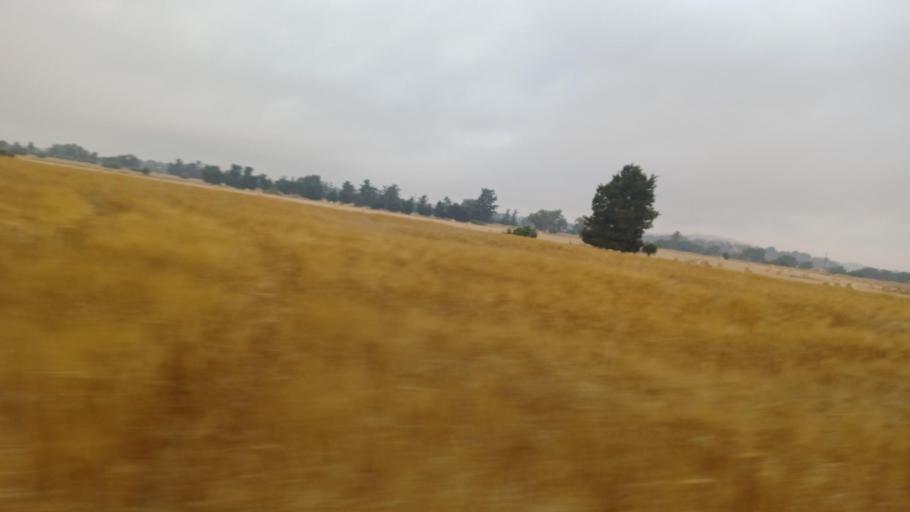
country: CY
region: Larnaka
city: Tersefanou
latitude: 34.8304
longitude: 33.5141
